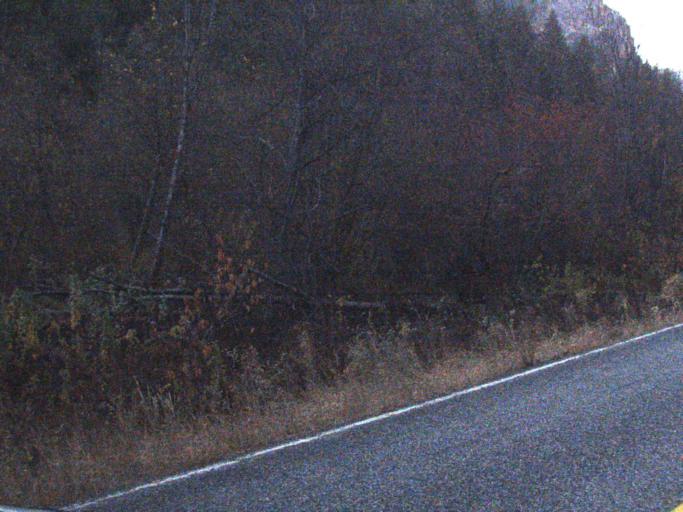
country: US
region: Washington
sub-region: Ferry County
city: Republic
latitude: 48.4974
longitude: -118.7412
